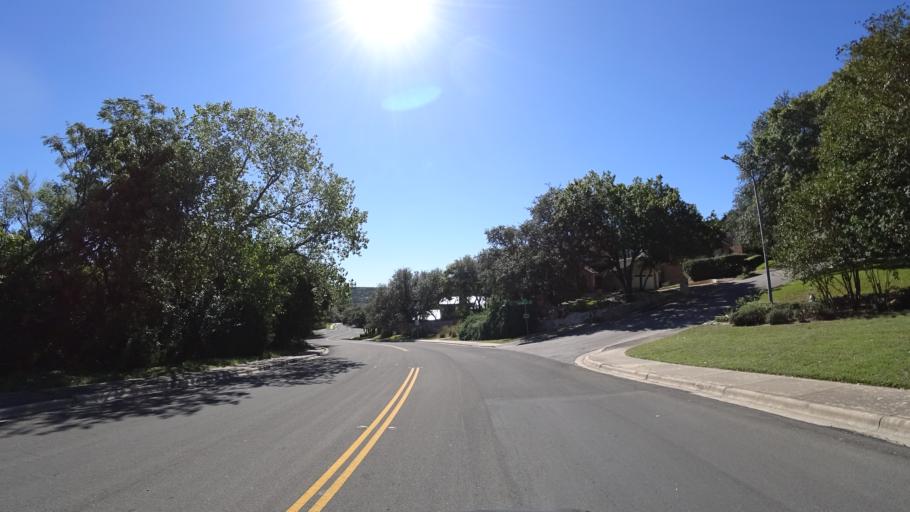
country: US
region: Texas
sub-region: Travis County
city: West Lake Hills
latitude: 30.3435
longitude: -97.7777
